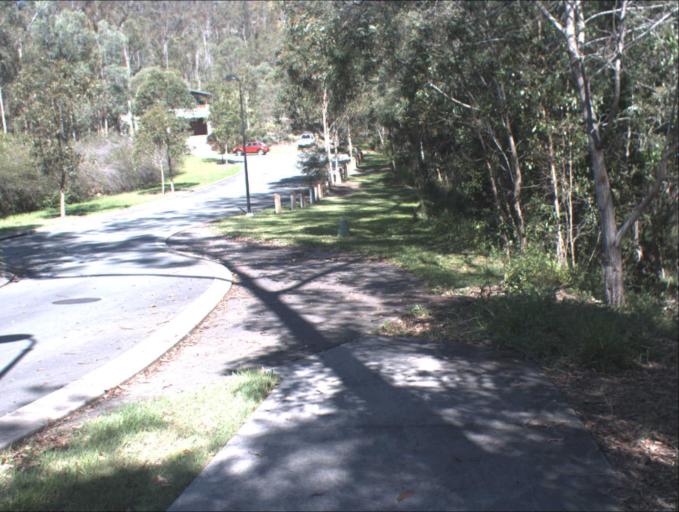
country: AU
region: Queensland
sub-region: Logan
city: Waterford West
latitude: -27.7147
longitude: 153.1559
